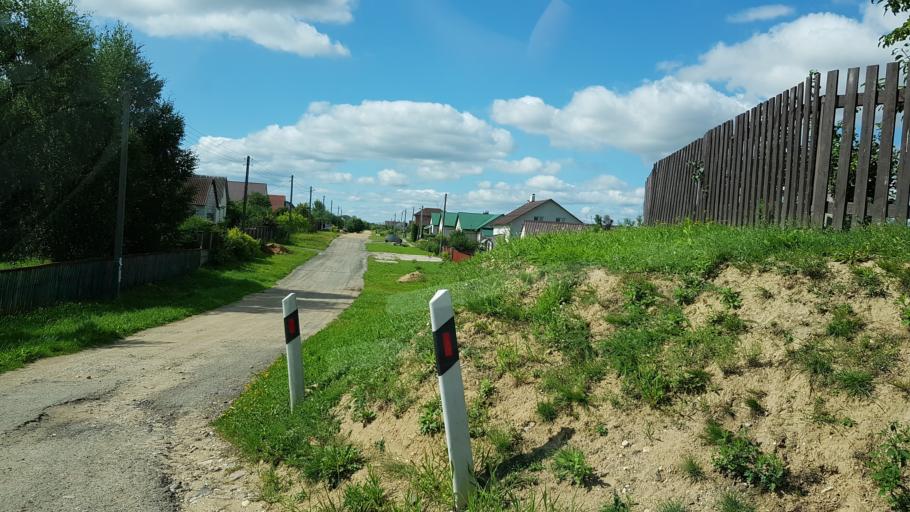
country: BY
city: Fanipol
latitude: 53.7599
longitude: 27.3299
